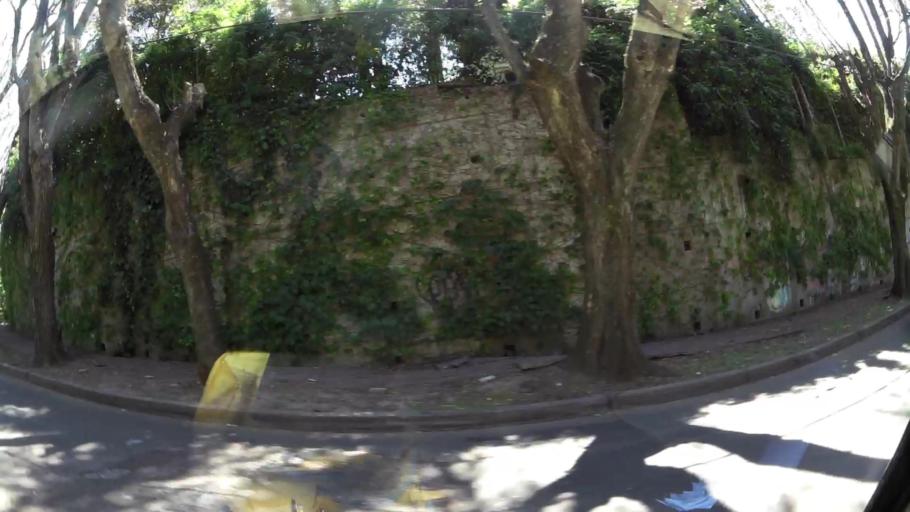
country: AR
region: Buenos Aires
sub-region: Partido de San Isidro
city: San Isidro
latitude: -34.4718
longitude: -58.4994
